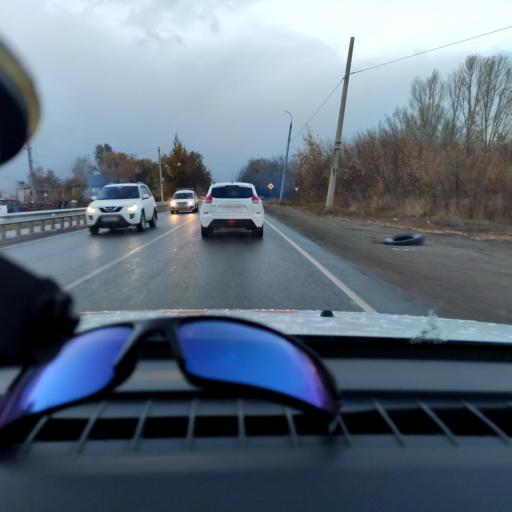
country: RU
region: Samara
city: Samara
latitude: 53.1313
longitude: 50.1079
